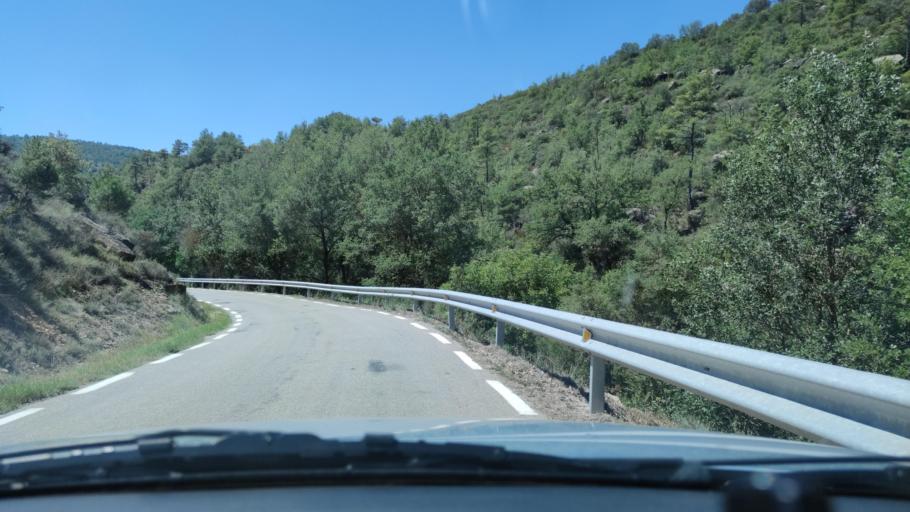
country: ES
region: Catalonia
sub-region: Provincia de Lleida
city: Tora de Riubregos
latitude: 41.8277
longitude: 1.4233
